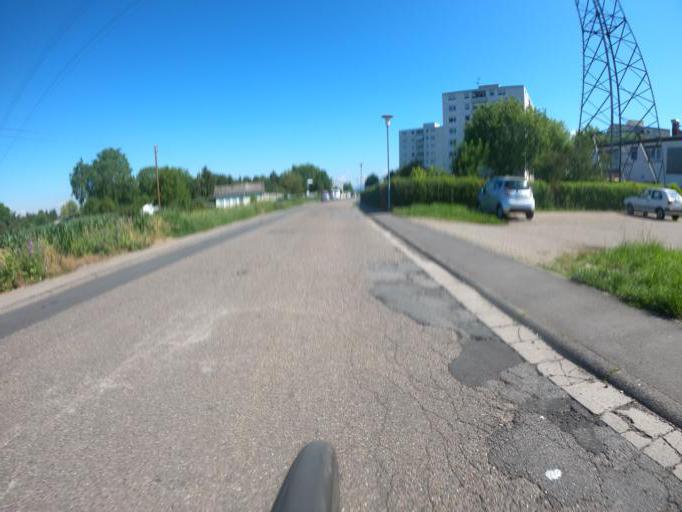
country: DE
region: Baden-Wuerttemberg
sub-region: Karlsruhe Region
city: Sandhausen
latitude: 49.3476
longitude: 8.6663
